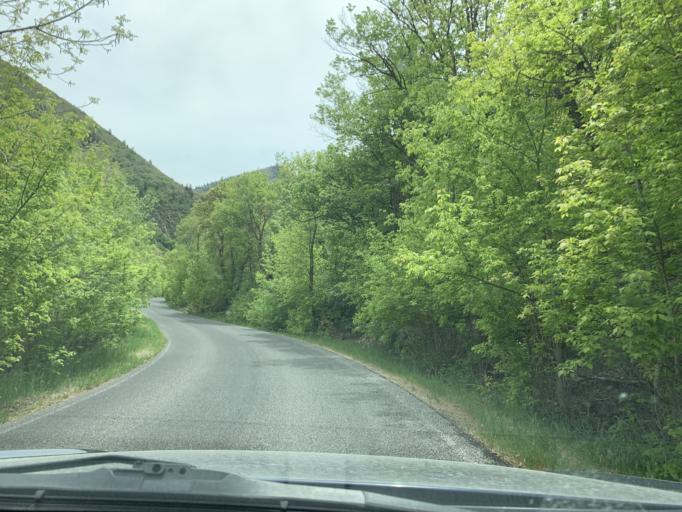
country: US
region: Utah
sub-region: Utah County
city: Mapleton
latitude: 40.1746
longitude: -111.4734
